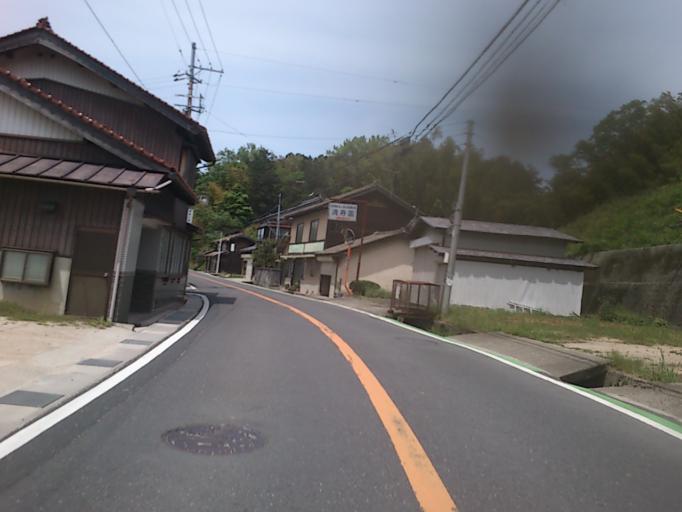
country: JP
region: Kyoto
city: Miyazu
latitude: 35.6613
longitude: 135.0923
